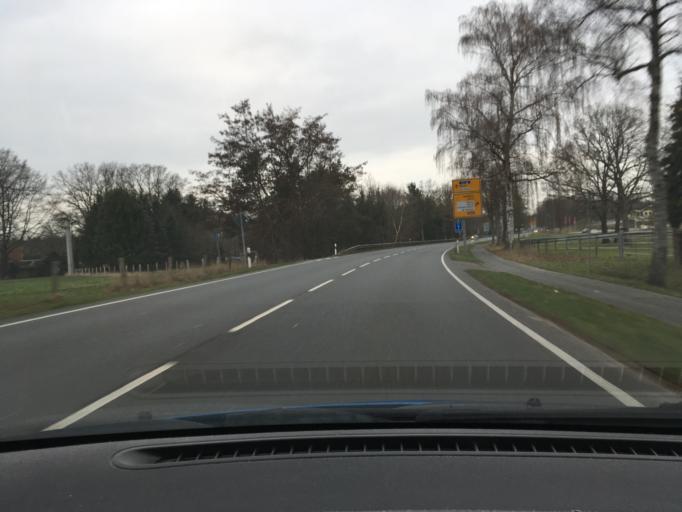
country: DE
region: Lower Saxony
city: Bomlitz
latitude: 52.8634
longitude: 9.6380
